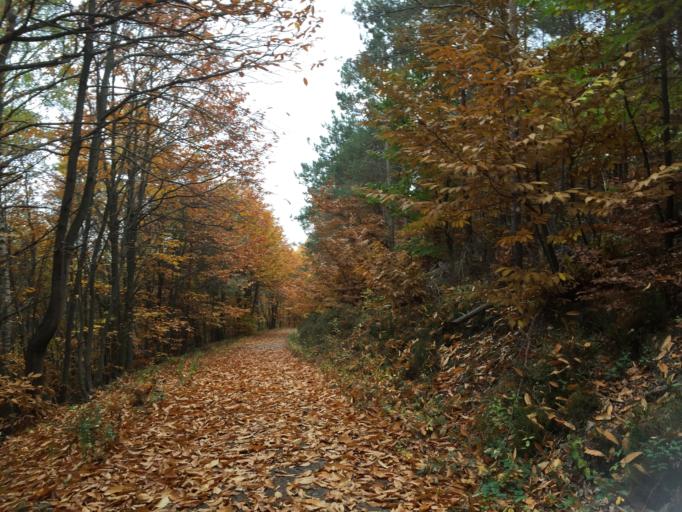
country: DE
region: Rheinland-Pfalz
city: Wachenheim
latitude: 49.4232
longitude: 8.1516
